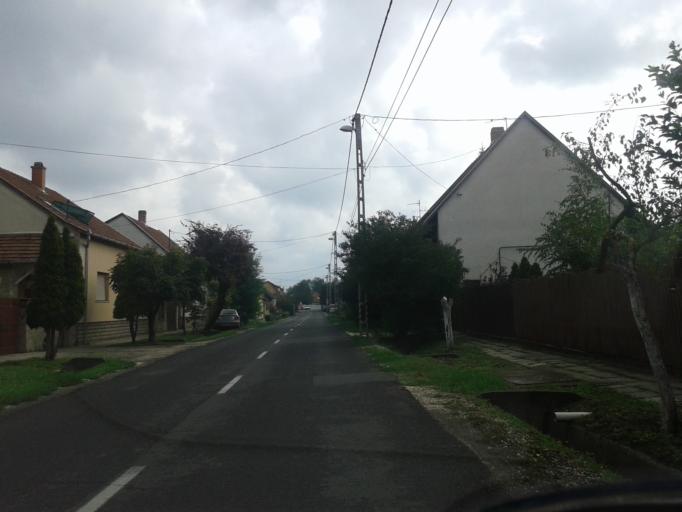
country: HU
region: Csongrad
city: Szeged
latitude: 46.2636
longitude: 20.1828
